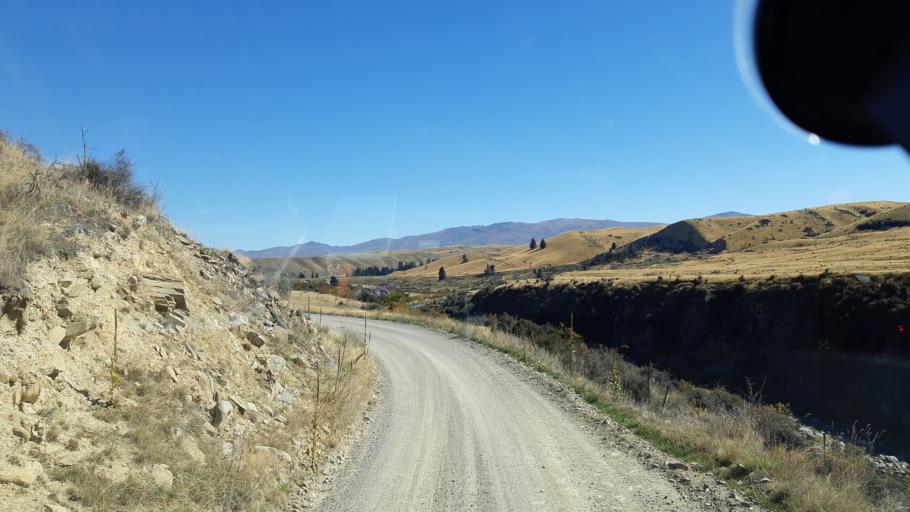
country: NZ
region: Otago
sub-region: Queenstown-Lakes District
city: Wanaka
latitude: -44.9048
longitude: 169.8742
